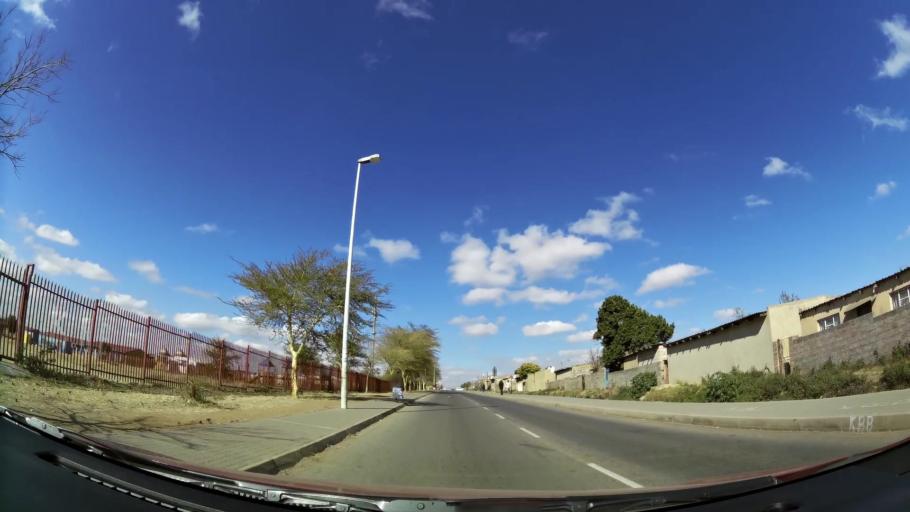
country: ZA
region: Gauteng
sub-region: City of Johannesburg Metropolitan Municipality
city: Modderfontein
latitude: -26.0402
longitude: 28.1814
